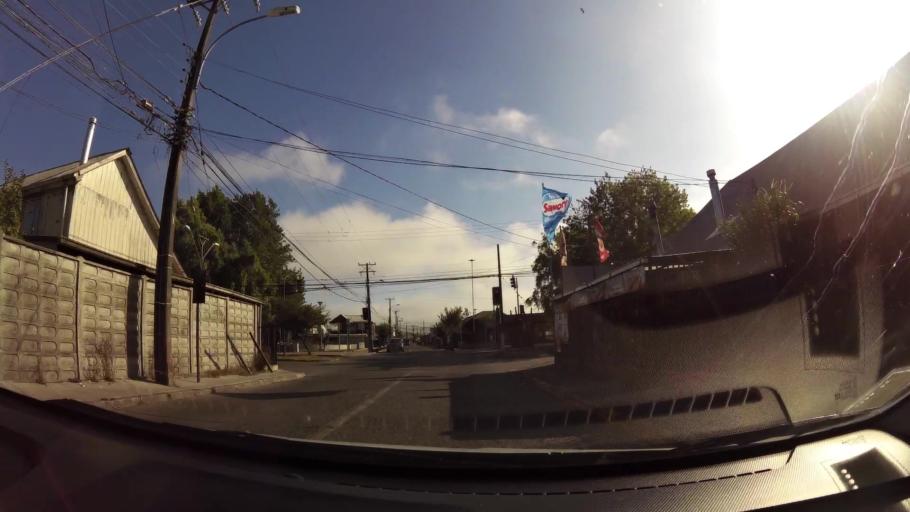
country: CL
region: Biobio
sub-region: Provincia de Concepcion
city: Concepcion
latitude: -36.7989
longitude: -73.0965
